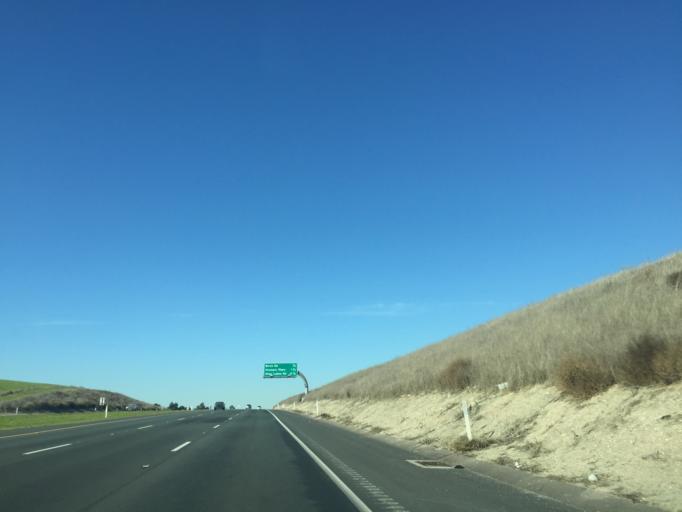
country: US
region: California
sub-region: San Diego County
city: Bonita
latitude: 32.6081
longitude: -116.9668
